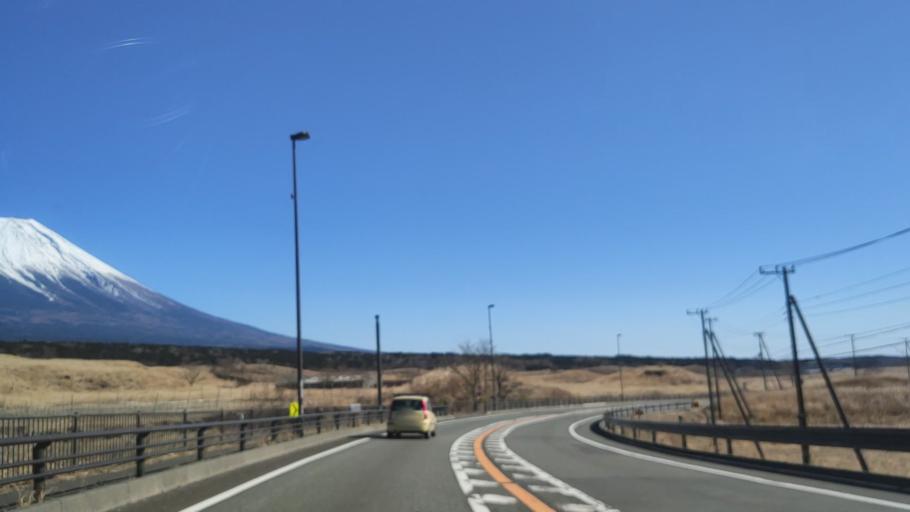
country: JP
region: Yamanashi
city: Fujikawaguchiko
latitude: 35.4258
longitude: 138.5927
